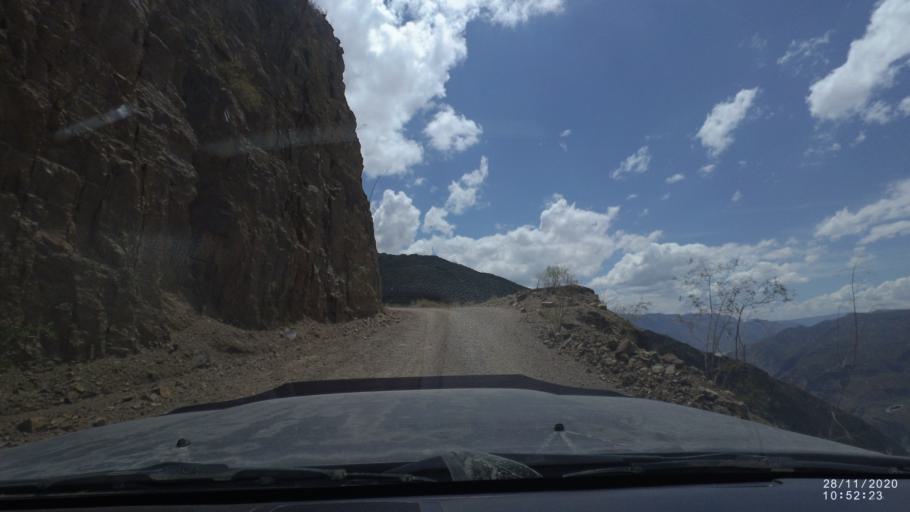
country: BO
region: Cochabamba
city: Capinota
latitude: -17.7851
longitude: -66.1196
